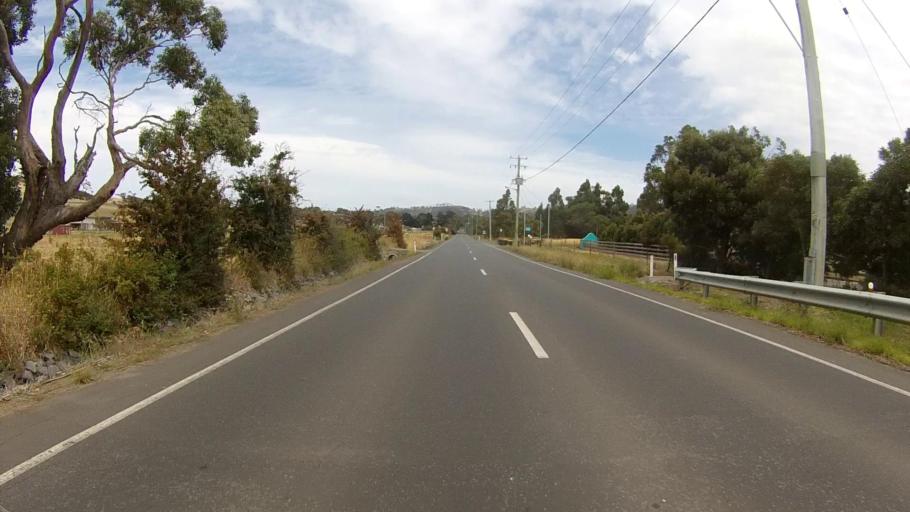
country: AU
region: Tasmania
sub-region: Clarence
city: Seven Mile Beach
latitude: -42.8616
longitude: 147.4931
